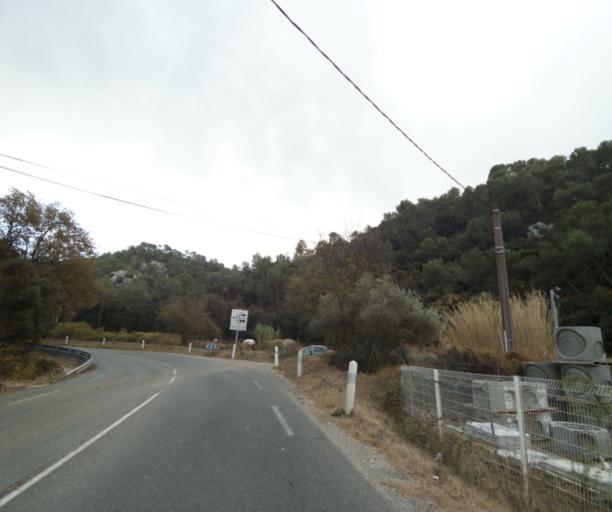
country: FR
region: Provence-Alpes-Cote d'Azur
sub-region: Departement des Bouches-du-Rhone
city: Gemenos
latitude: 43.2678
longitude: 5.6486
